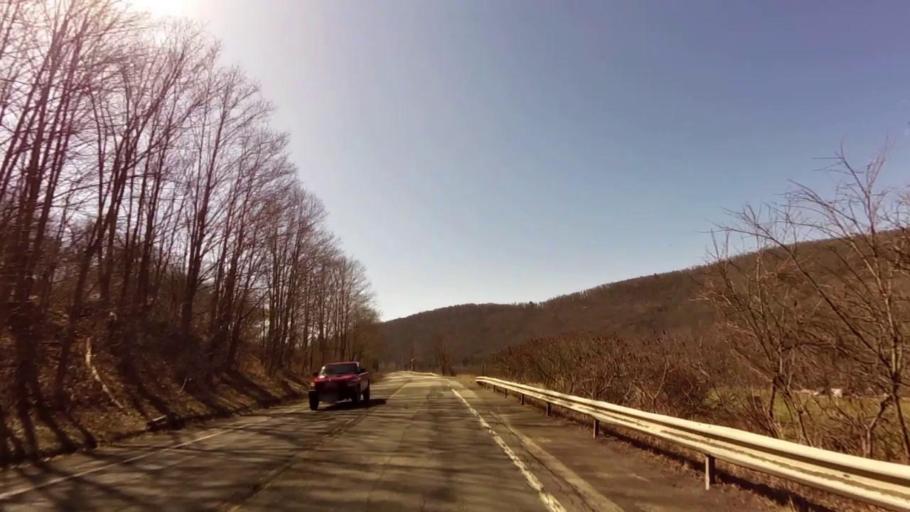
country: US
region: New York
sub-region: Cattaraugus County
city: Franklinville
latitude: 42.3196
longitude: -78.4612
